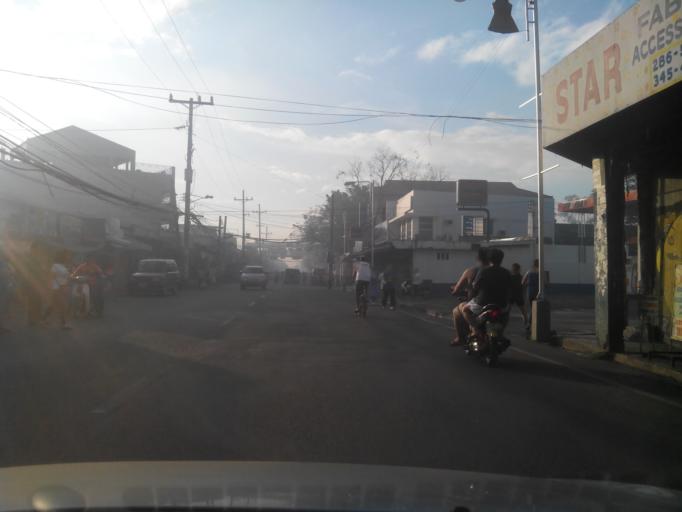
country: PH
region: Calabarzon
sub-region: Province of Rizal
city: Taytay
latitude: 14.5642
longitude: 121.1328
